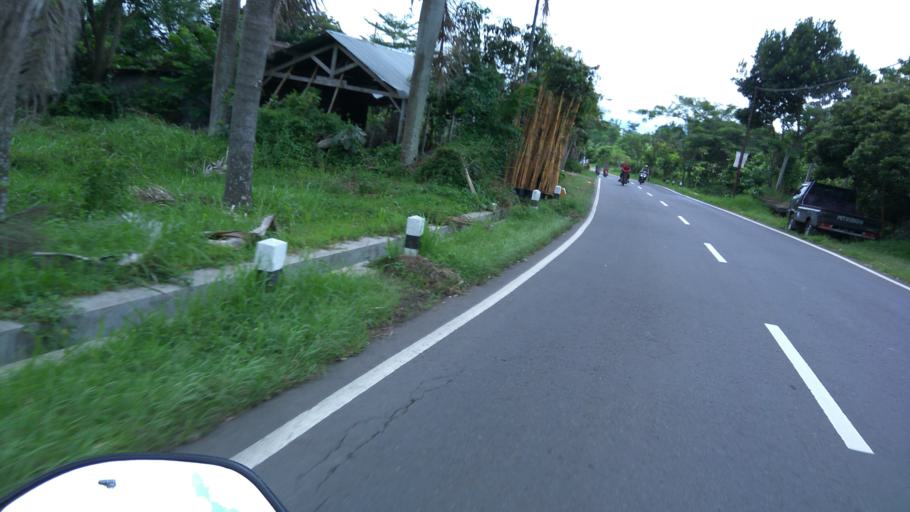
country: ID
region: Central Java
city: Ambarawa
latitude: -7.2368
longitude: 110.3855
